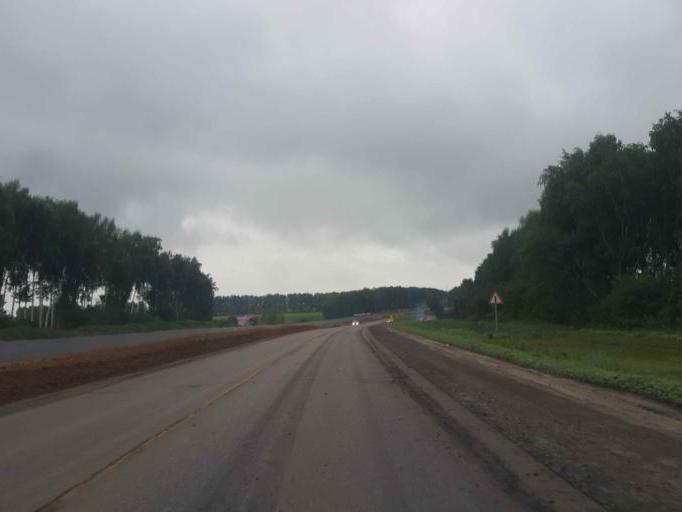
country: RU
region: Tambov
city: Selezni
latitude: 52.7711
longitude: 41.0513
